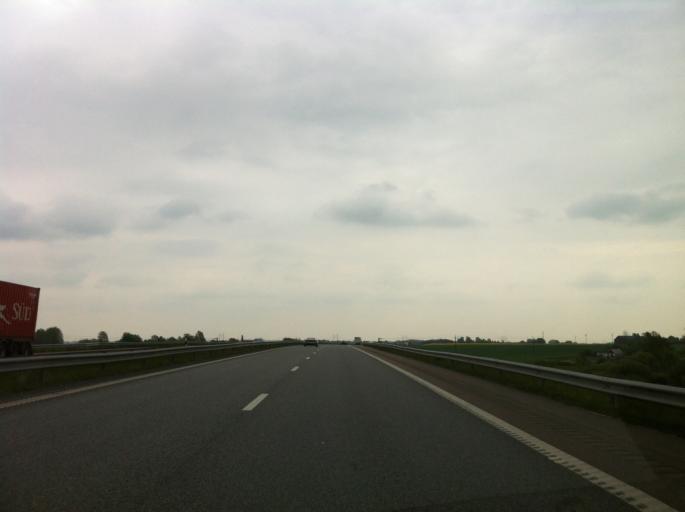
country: SE
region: Skane
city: Bjarred
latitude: 55.7352
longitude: 13.0681
